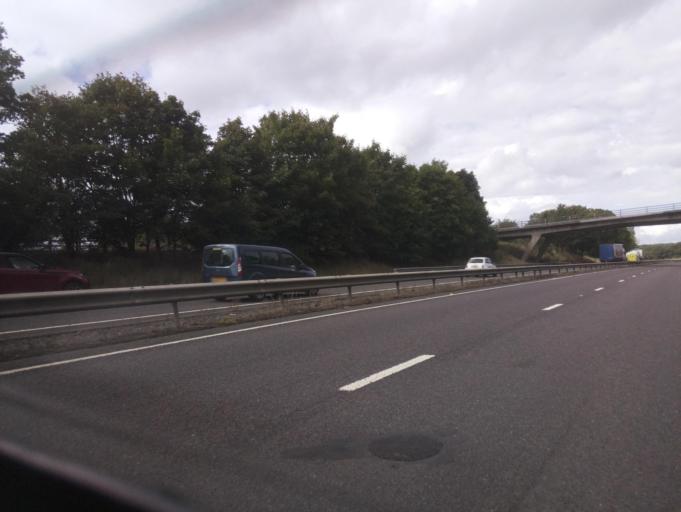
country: GB
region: England
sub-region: Northumberland
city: Corbridge
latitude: 54.9739
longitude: -1.9828
